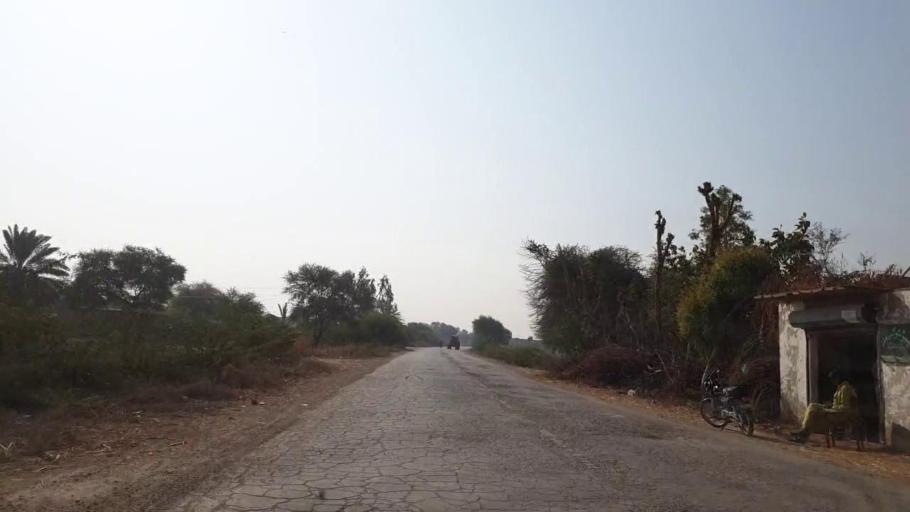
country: PK
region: Sindh
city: Mirpur Khas
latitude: 25.5390
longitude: 69.0446
